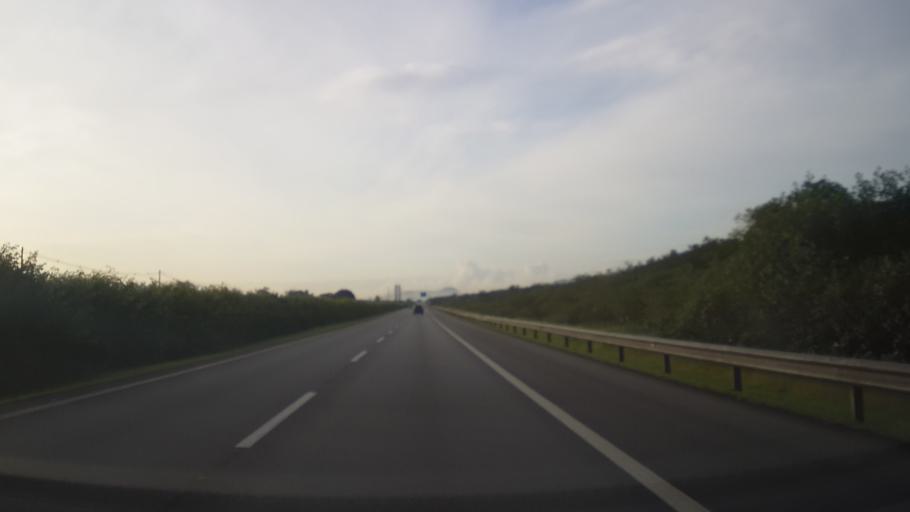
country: BR
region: Sao Paulo
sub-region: Cubatao
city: Cubatao
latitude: -23.9116
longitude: -46.4442
